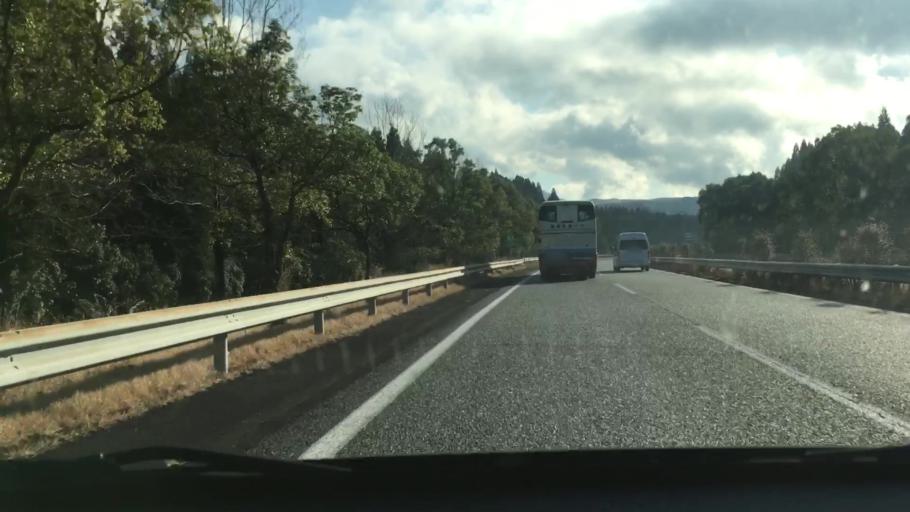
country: JP
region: Kagoshima
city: Okuchi-shinohara
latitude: 32.0321
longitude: 130.7982
